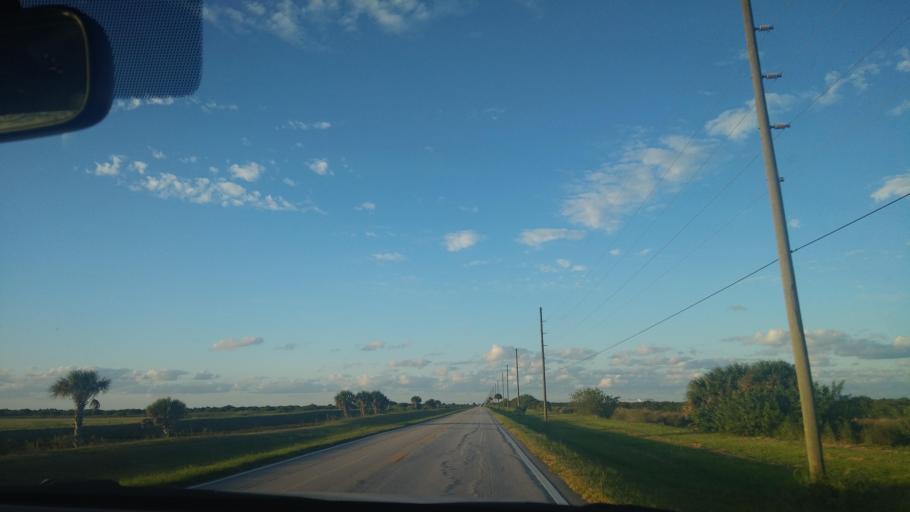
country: US
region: Florida
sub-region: Indian River County
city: Fellsmere
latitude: 27.7108
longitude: -80.6428
